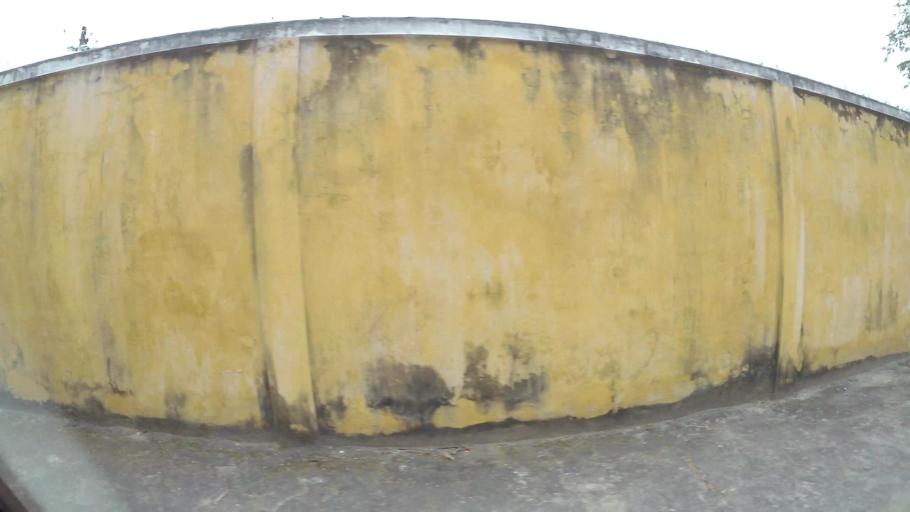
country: VN
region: Da Nang
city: Cam Le
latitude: 16.0418
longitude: 108.2059
